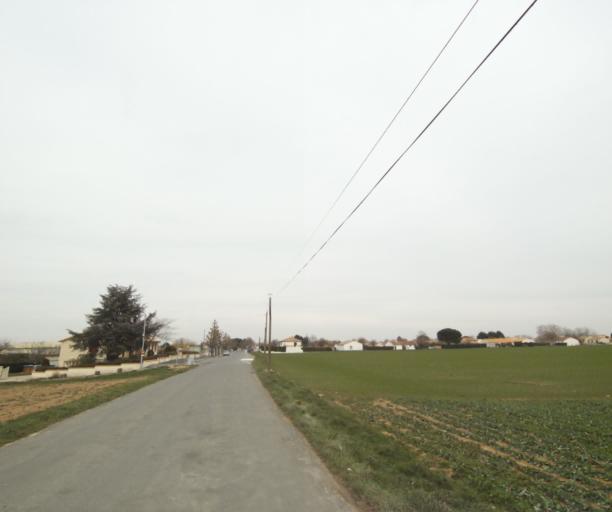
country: FR
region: Poitou-Charentes
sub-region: Departement des Deux-Sevres
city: Bessines
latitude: 46.3152
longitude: -0.5178
